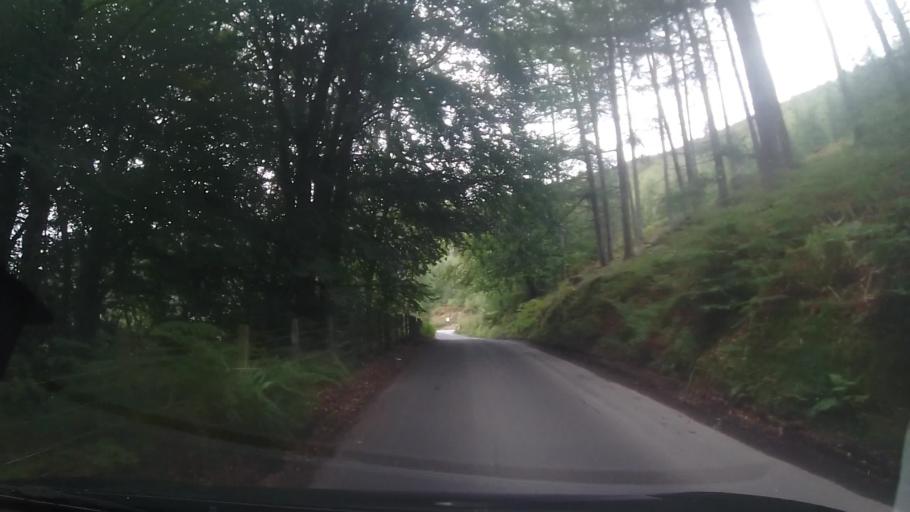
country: GB
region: Wales
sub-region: Sir Powys
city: Rhayader
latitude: 52.2678
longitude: -3.5933
